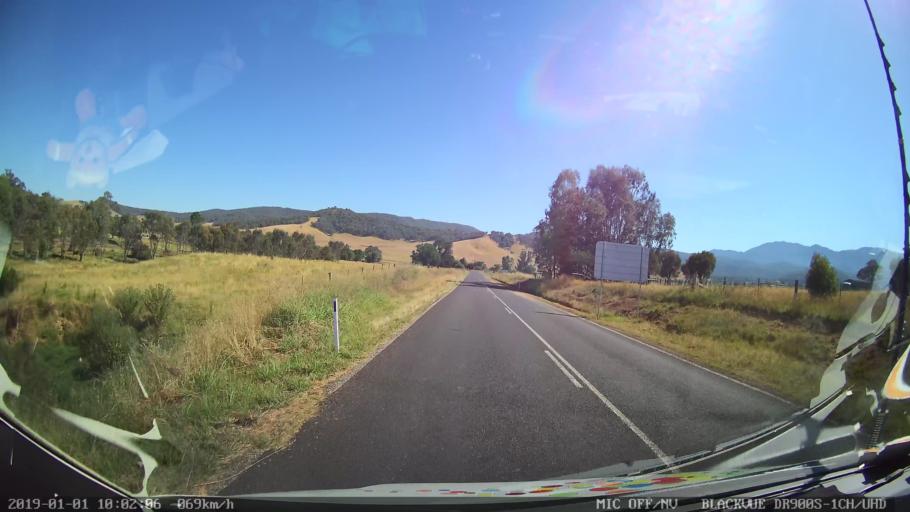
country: AU
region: New South Wales
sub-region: Snowy River
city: Jindabyne
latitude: -36.1846
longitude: 148.1014
